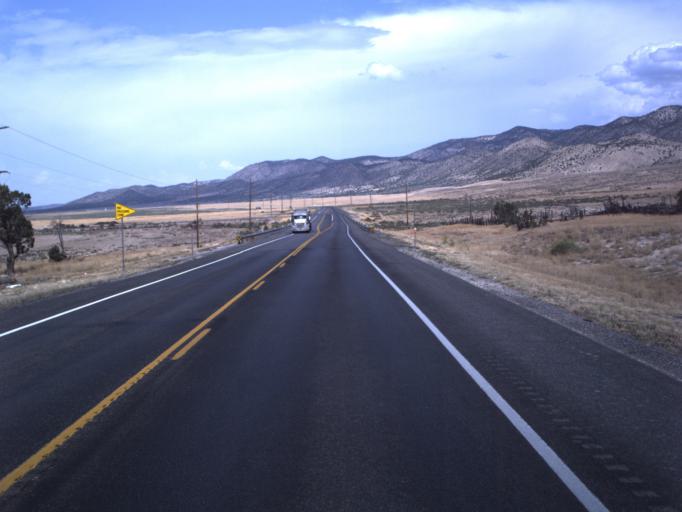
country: US
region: Utah
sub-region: Sanpete County
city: Gunnison
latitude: 39.2256
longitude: -111.8480
